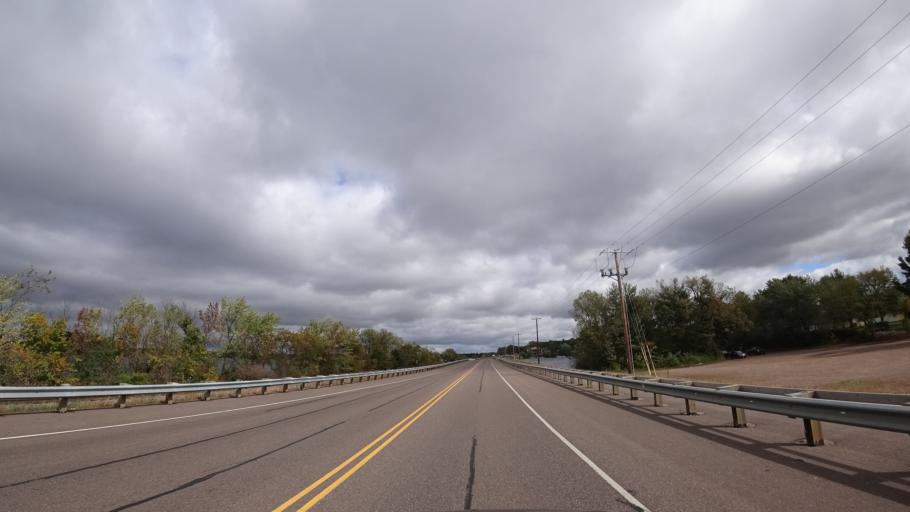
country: US
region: Wisconsin
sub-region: Chippewa County
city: Lake Wissota
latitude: 44.9250
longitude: -91.3184
